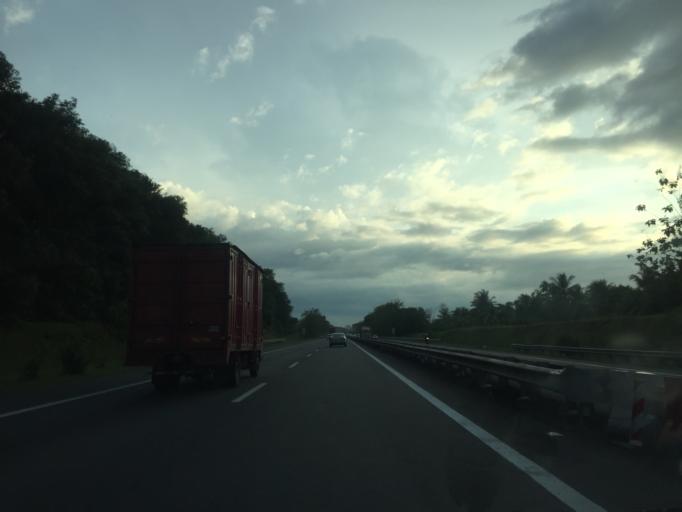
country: MY
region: Kedah
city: Sungai Petani
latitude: 5.6676
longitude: 100.5135
